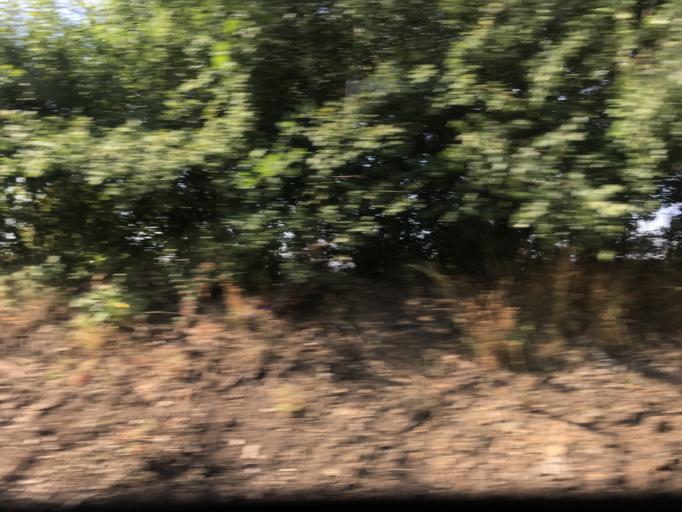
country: CZ
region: Jihocesky
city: Chotoviny
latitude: 49.5359
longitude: 14.6505
